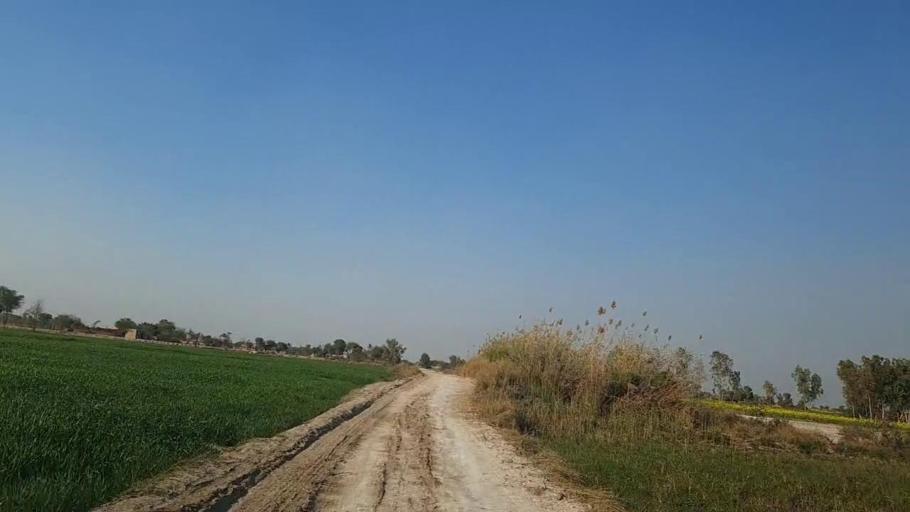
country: PK
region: Sindh
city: Daur
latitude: 26.3277
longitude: 68.1772
